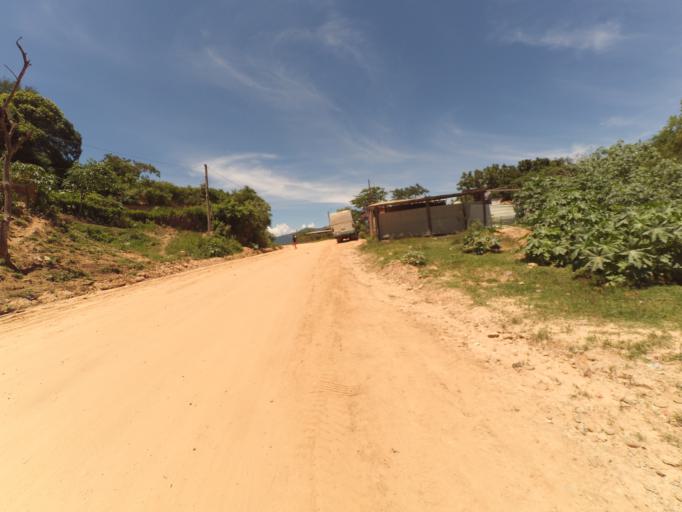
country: BO
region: Chuquisaca
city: Monteagudo
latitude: -19.8046
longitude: -63.9535
